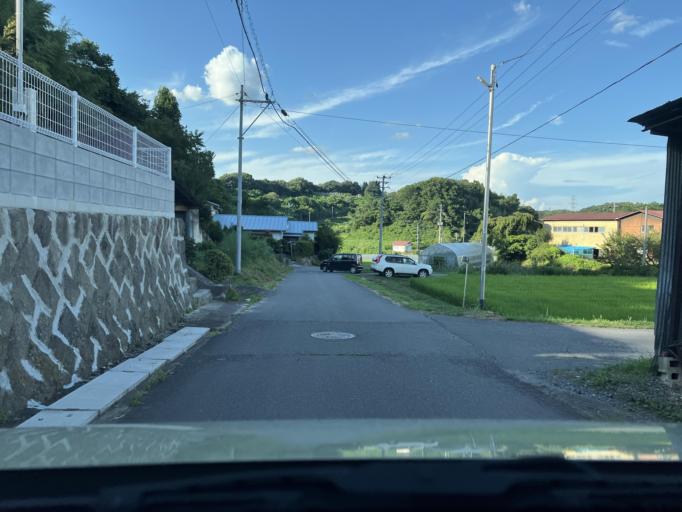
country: JP
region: Fukushima
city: Miharu
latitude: 37.4269
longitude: 140.4408
